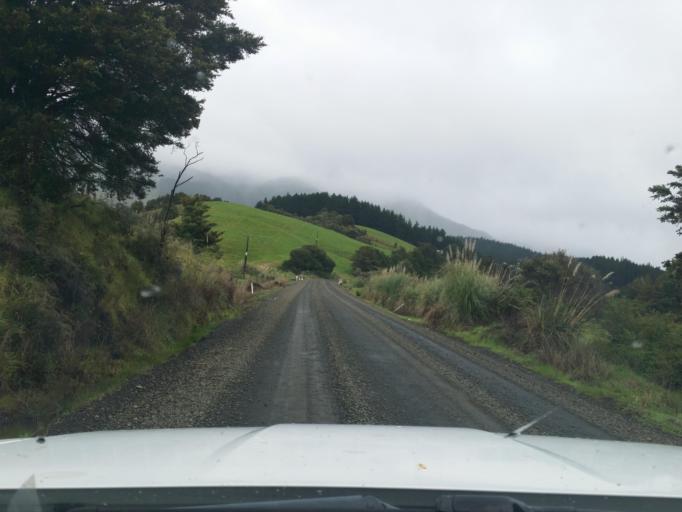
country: NZ
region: Northland
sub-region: Kaipara District
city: Dargaville
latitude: -35.8084
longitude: 173.9975
